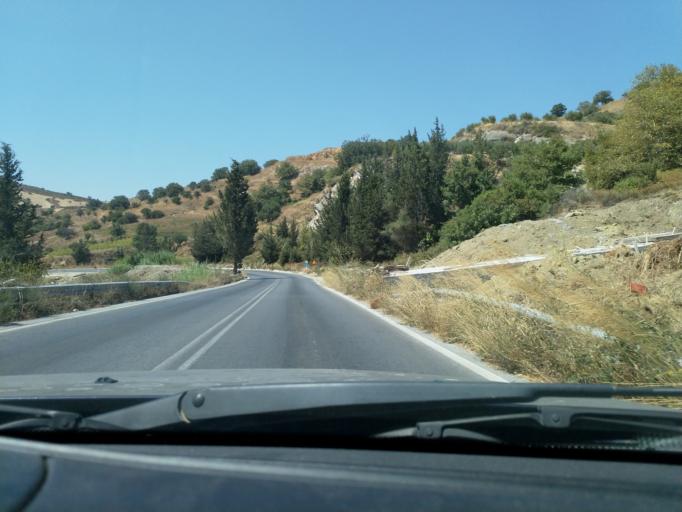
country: GR
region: Crete
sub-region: Nomos Rethymnis
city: Atsipopoulon
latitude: 35.2578
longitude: 24.4748
